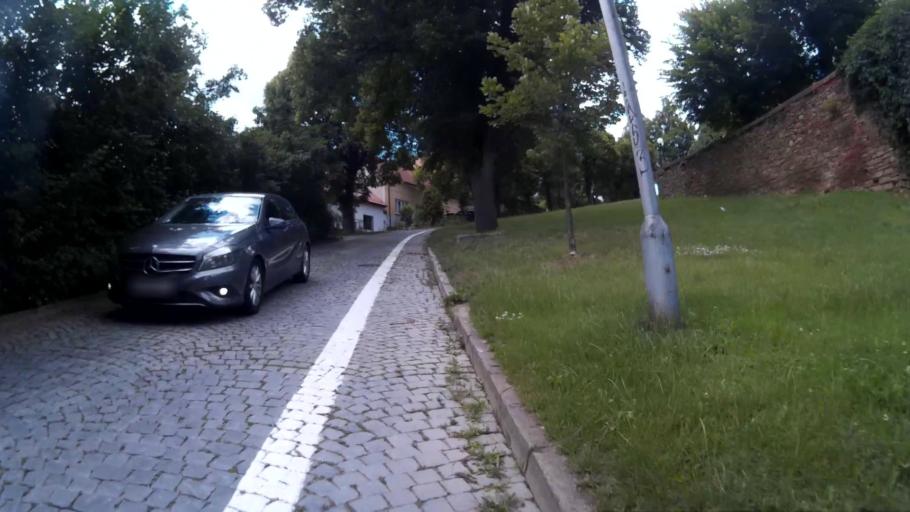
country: CZ
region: South Moravian
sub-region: Okres Brno-Venkov
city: Rosice
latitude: 49.1811
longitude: 16.3871
